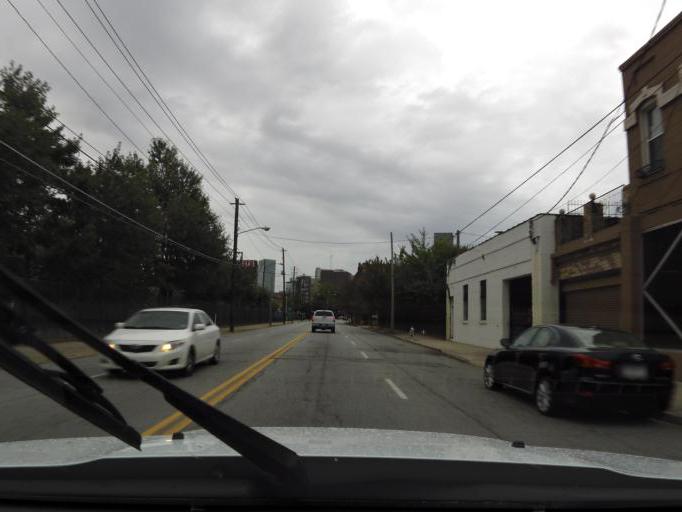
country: US
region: Georgia
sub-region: Fulton County
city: Atlanta
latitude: 33.7676
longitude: -84.3980
